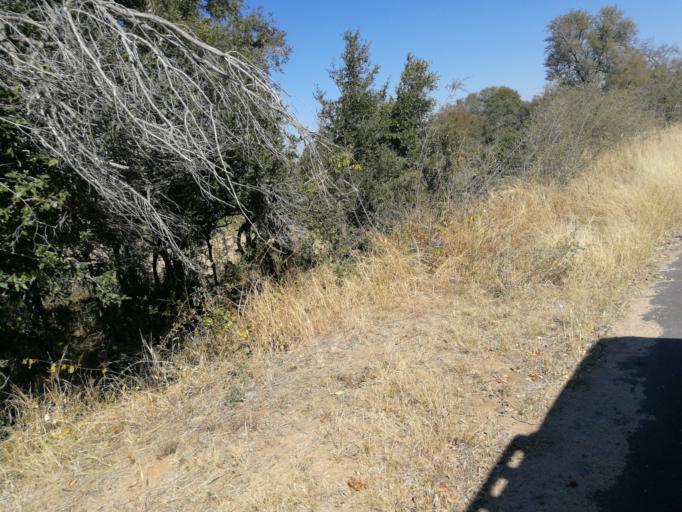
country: ZA
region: Limpopo
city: Thulamahashi
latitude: -24.9423
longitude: 31.6780
